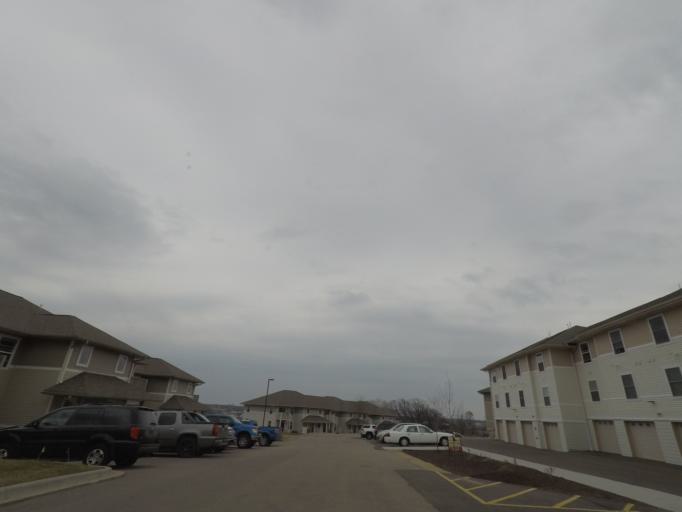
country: US
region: Wisconsin
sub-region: Dane County
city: Middleton
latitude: 43.1071
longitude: -89.5387
